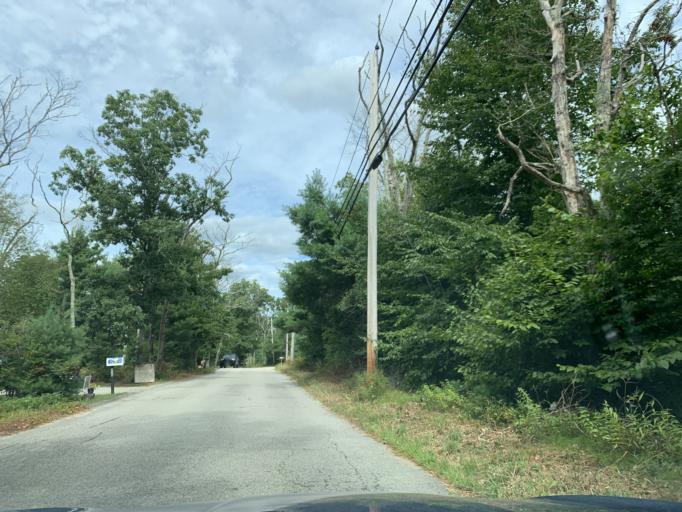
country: US
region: Rhode Island
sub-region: Washington County
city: Exeter
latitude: 41.5476
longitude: -71.6175
